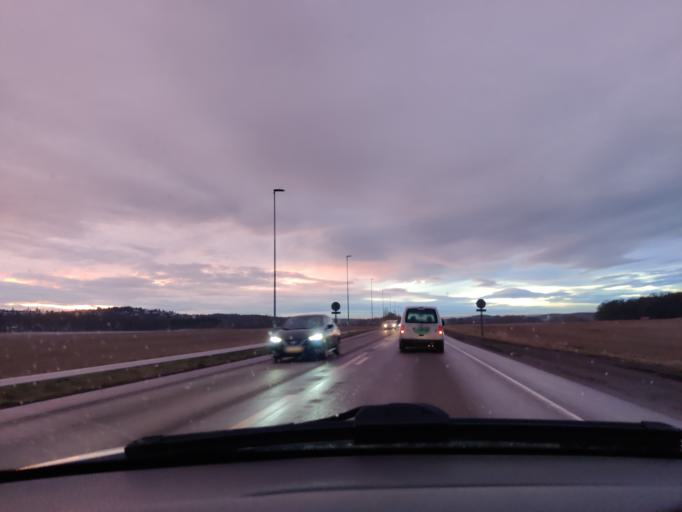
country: NO
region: Vestfold
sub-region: Tonsberg
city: Tonsberg
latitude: 59.2820
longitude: 10.3877
